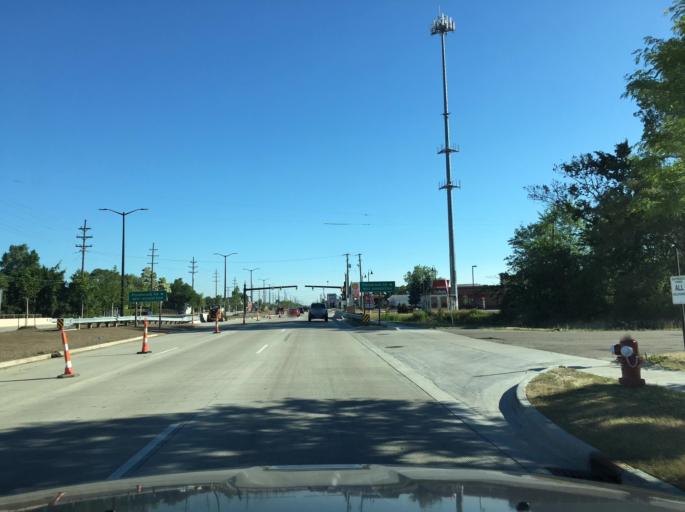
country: US
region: Michigan
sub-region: Macomb County
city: Sterling Heights
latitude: 42.5829
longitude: -83.0301
